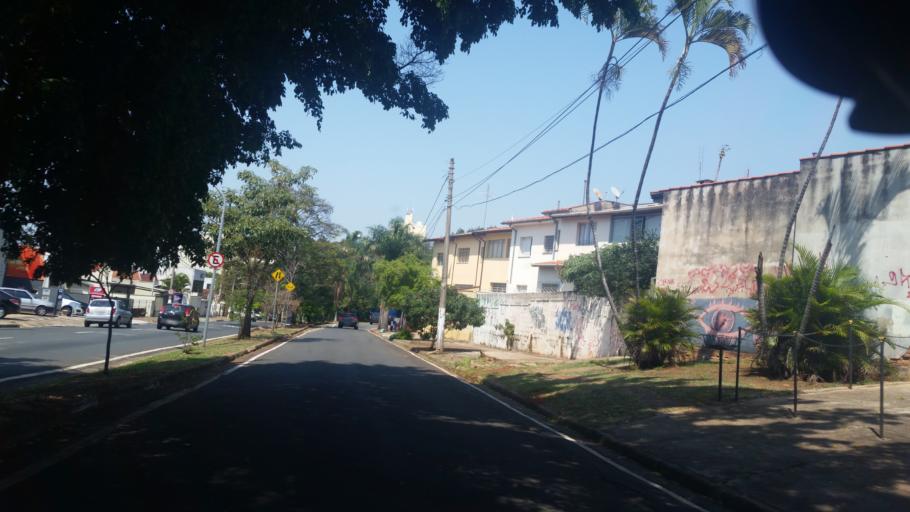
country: BR
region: Sao Paulo
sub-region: Campinas
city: Campinas
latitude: -22.8769
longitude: -47.0677
